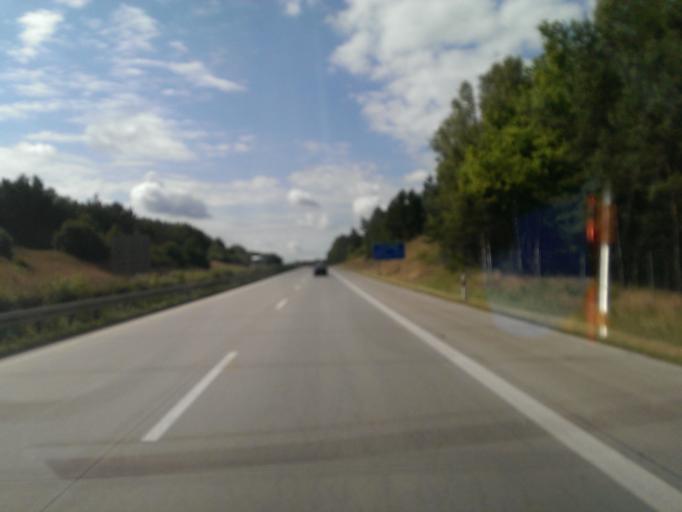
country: DE
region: Brandenburg
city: Teupitz
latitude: 52.1164
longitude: 13.6462
